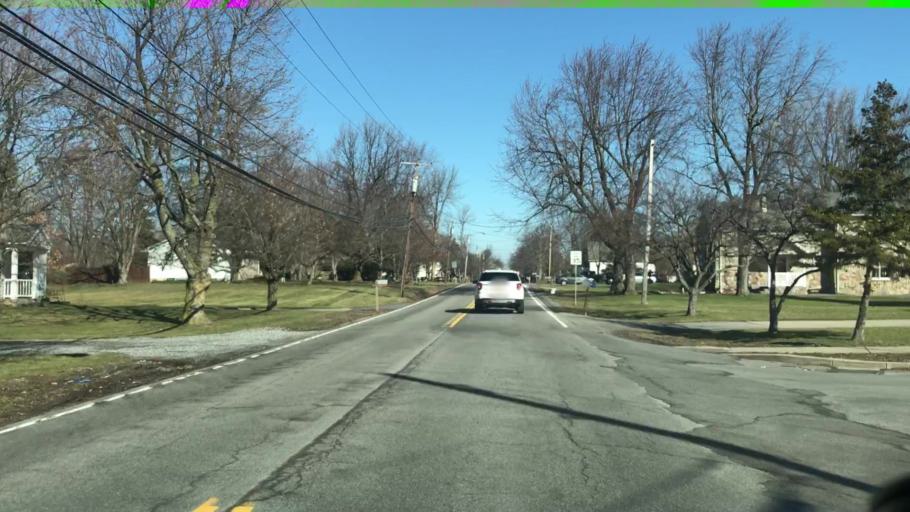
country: US
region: New York
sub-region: Erie County
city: Lancaster
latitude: 42.8706
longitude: -78.6764
